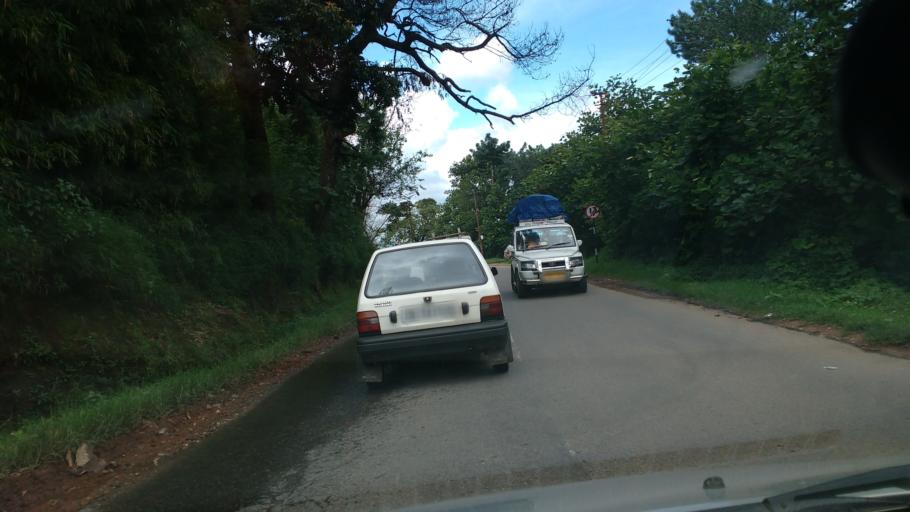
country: IN
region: Meghalaya
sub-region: East Khasi Hills
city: Shillong
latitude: 25.5616
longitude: 91.8533
